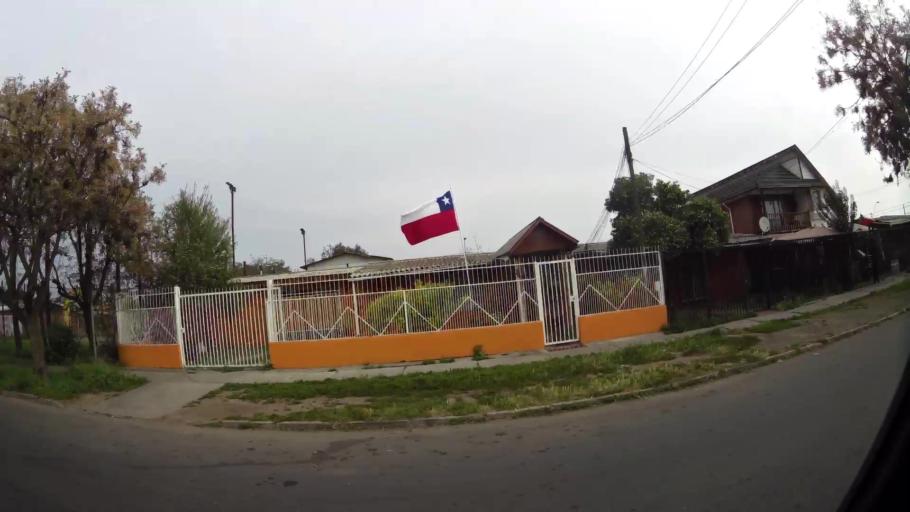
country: CL
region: Santiago Metropolitan
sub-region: Provincia de Santiago
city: Lo Prado
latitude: -33.5241
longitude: -70.7625
